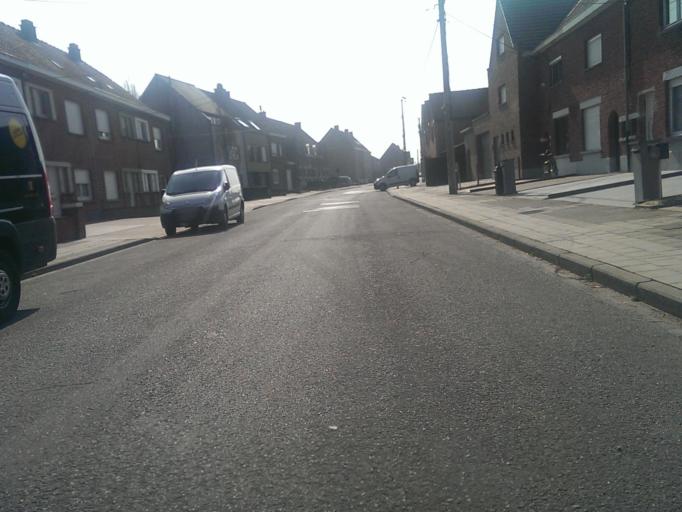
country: BE
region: Flanders
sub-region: Provincie West-Vlaanderen
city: Roeselare
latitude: 50.9338
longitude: 3.1243
